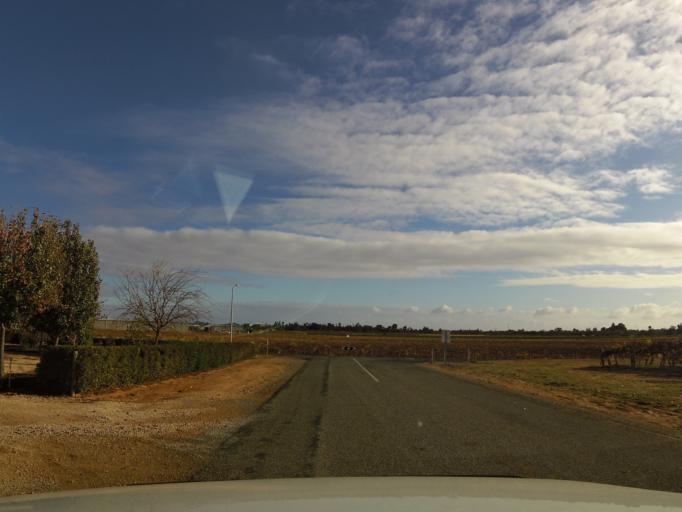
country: AU
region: South Australia
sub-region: Berri and Barmera
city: Berri
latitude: -34.2787
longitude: 140.5825
